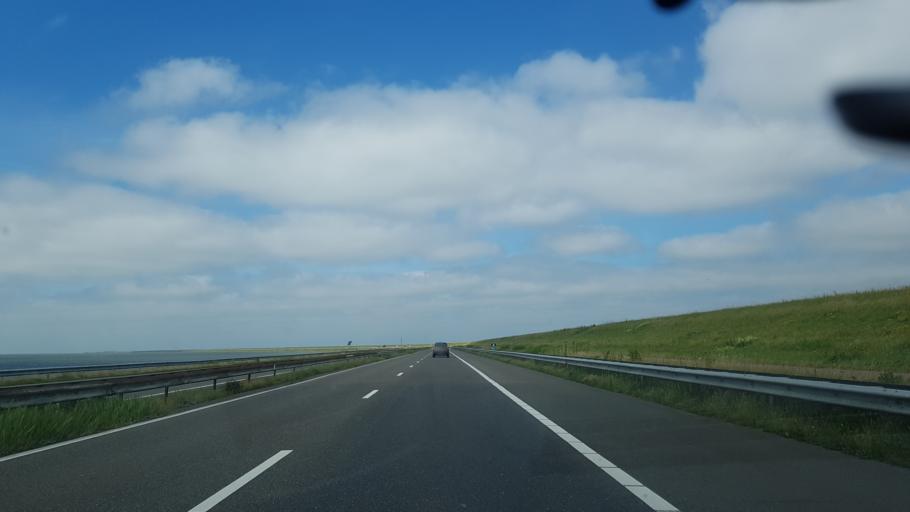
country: NL
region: Friesland
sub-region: Sudwest Fryslan
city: Makkum
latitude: 53.0704
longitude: 5.3102
